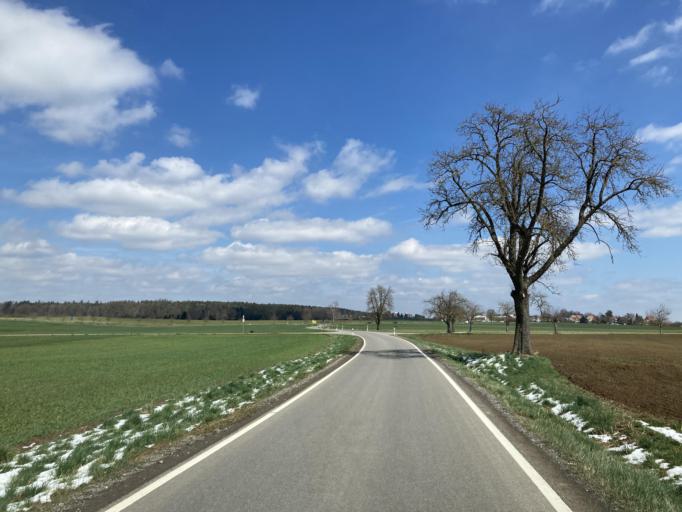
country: DE
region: Baden-Wuerttemberg
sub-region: Tuebingen Region
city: Haigerloch
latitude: 48.4189
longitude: 8.8275
